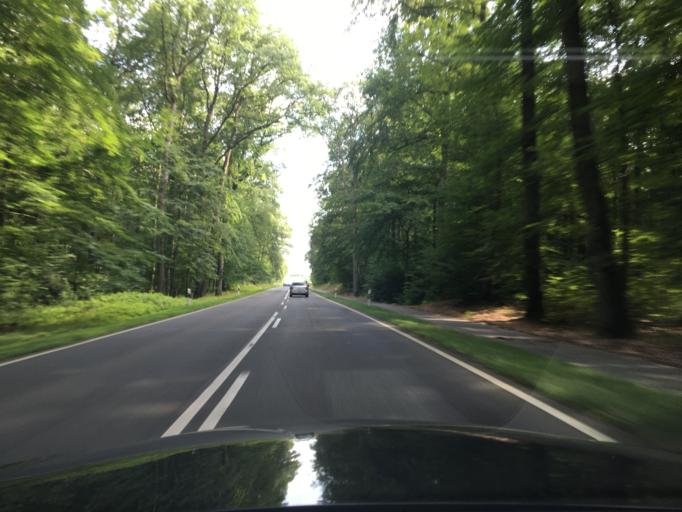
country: DE
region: Mecklenburg-Vorpommern
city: Neustrelitz
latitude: 53.4172
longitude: 13.0411
